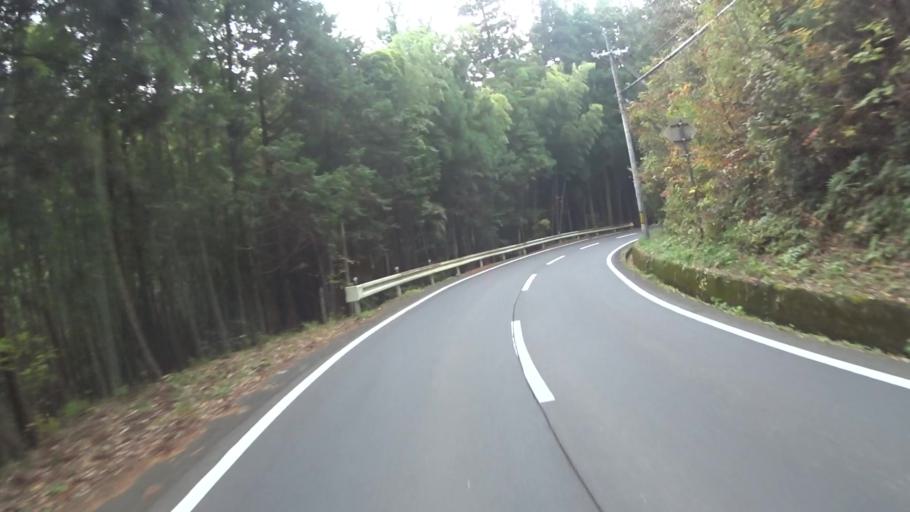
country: JP
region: Kyoto
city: Maizuru
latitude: 35.5350
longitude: 135.4425
